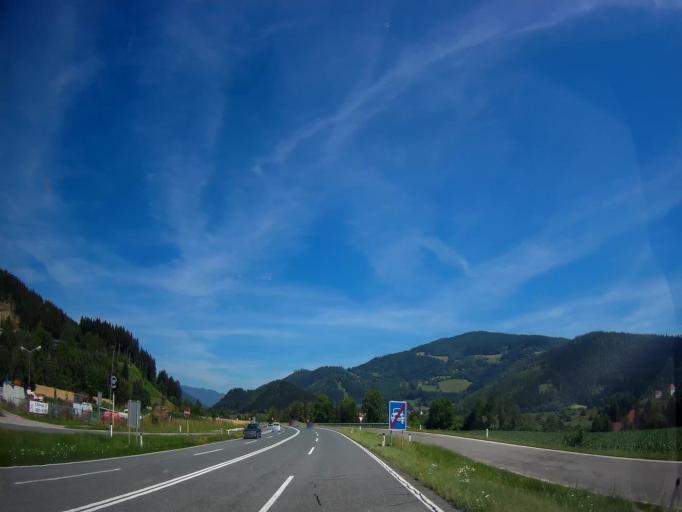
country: AT
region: Carinthia
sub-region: Politischer Bezirk Sankt Veit an der Glan
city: Althofen
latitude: 46.8754
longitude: 14.4511
